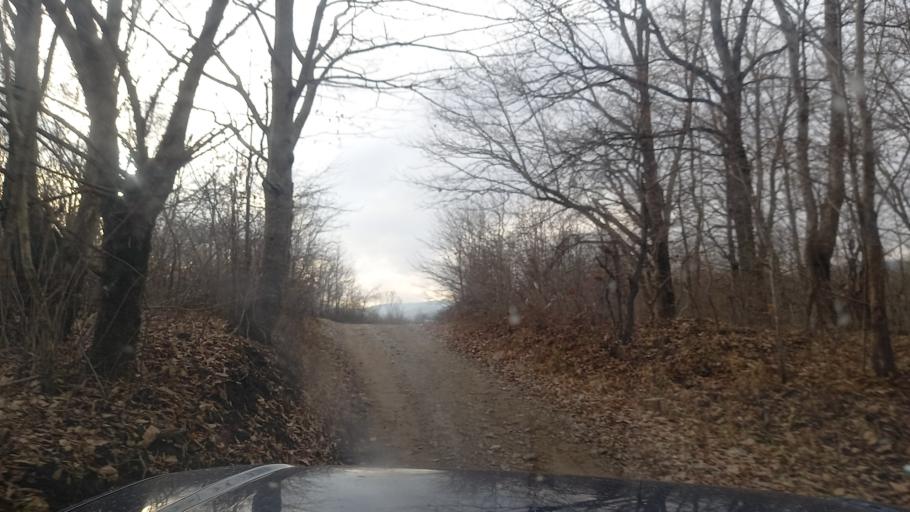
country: RU
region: Krasnodarskiy
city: Neftegorsk
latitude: 44.2410
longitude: 39.7616
